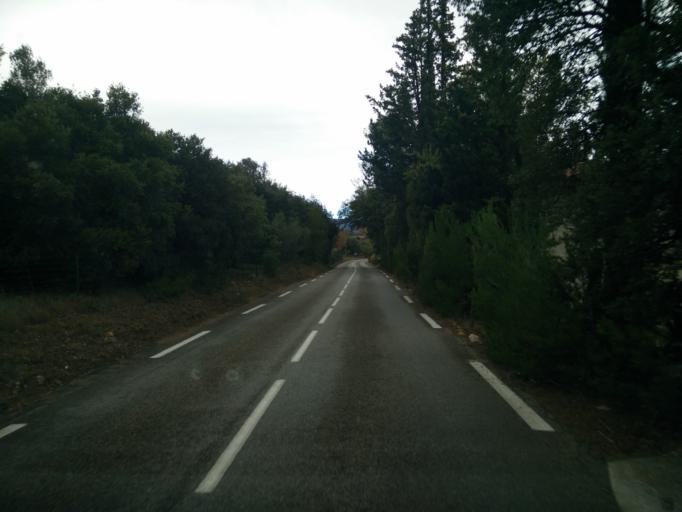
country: FR
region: Provence-Alpes-Cote d'Azur
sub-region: Departement du Var
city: Carces
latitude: 43.4779
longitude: 6.1371
